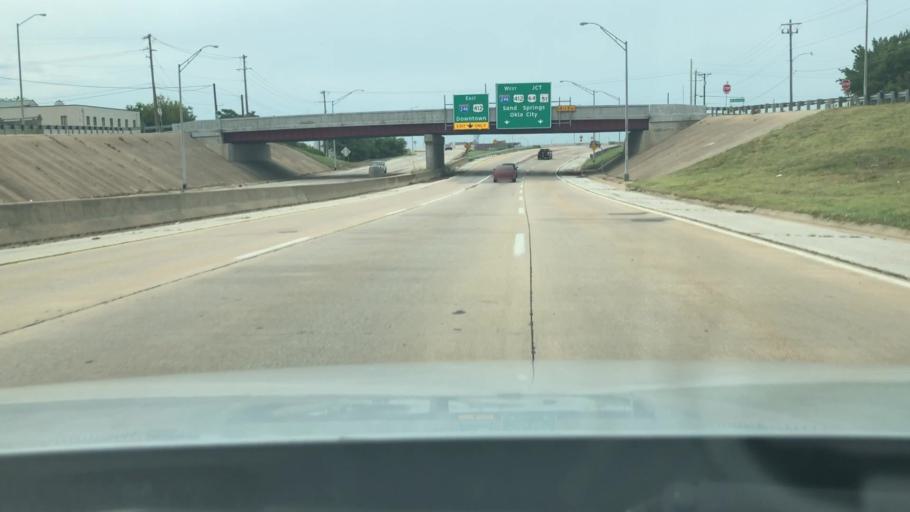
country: US
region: Oklahoma
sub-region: Tulsa County
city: Tulsa
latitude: 36.1634
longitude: -96.0008
